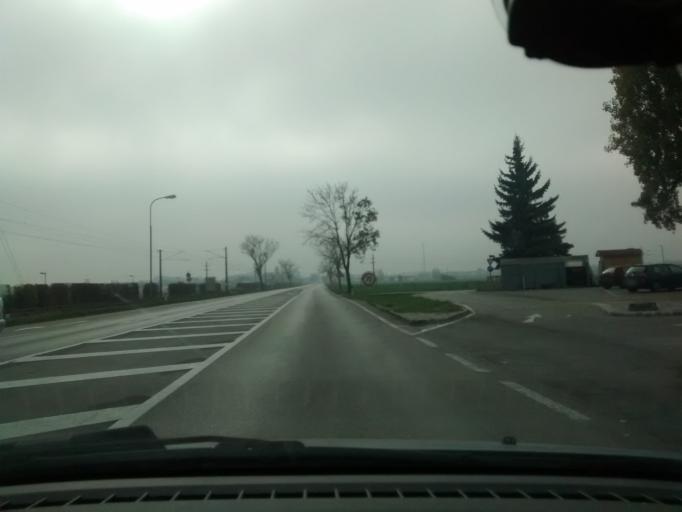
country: AT
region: Lower Austria
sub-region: Politischer Bezirk Modling
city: Guntramsdorf
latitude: 48.0358
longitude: 16.3026
